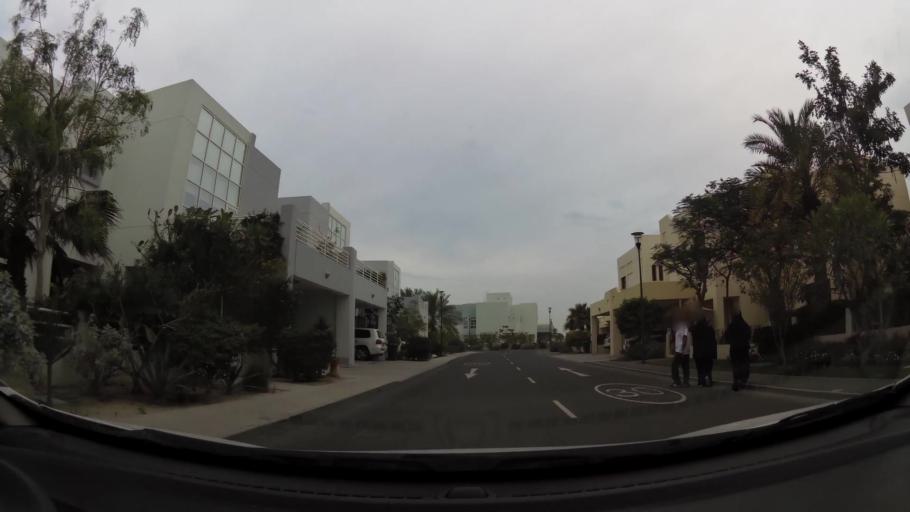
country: BH
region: Northern
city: Ar Rifa'
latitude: 26.0999
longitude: 50.5672
